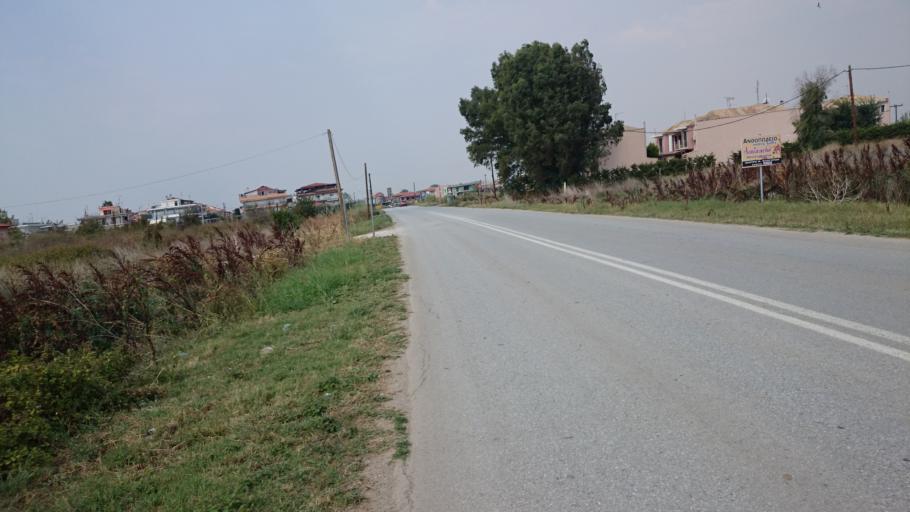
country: GR
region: Central Macedonia
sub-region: Nomos Chalkidikis
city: Nea Moudhania
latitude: 40.2502
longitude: 23.2570
